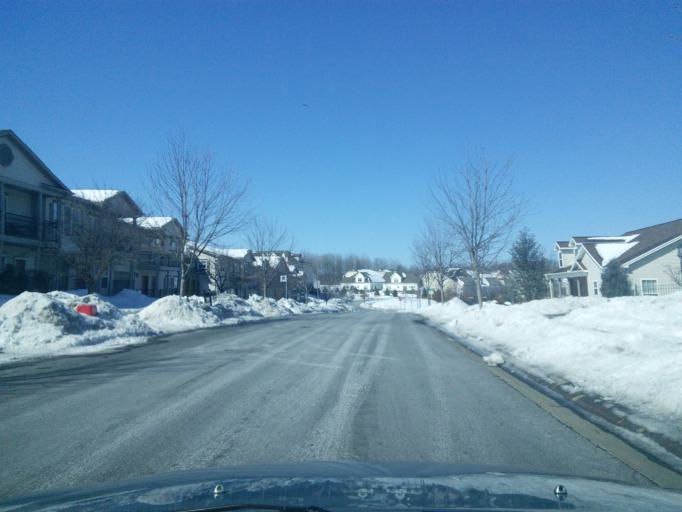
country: US
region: Pennsylvania
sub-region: Centre County
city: State College
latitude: 40.8261
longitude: -77.8787
